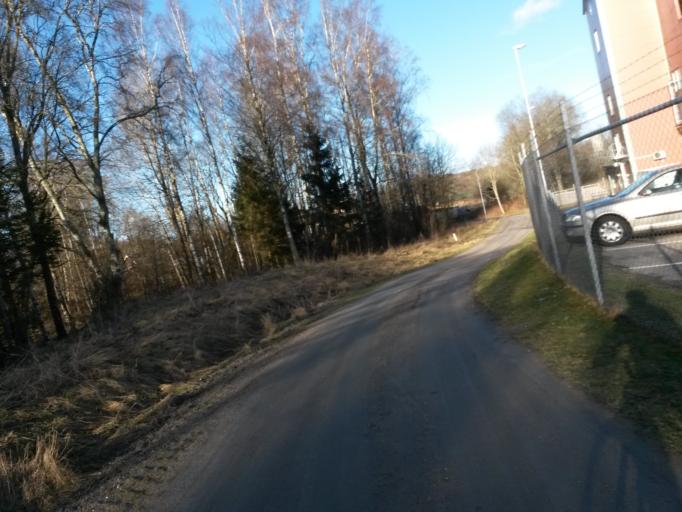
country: SE
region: Vaestra Goetaland
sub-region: Vargarda Kommun
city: Vargarda
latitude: 58.0240
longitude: 12.7875
